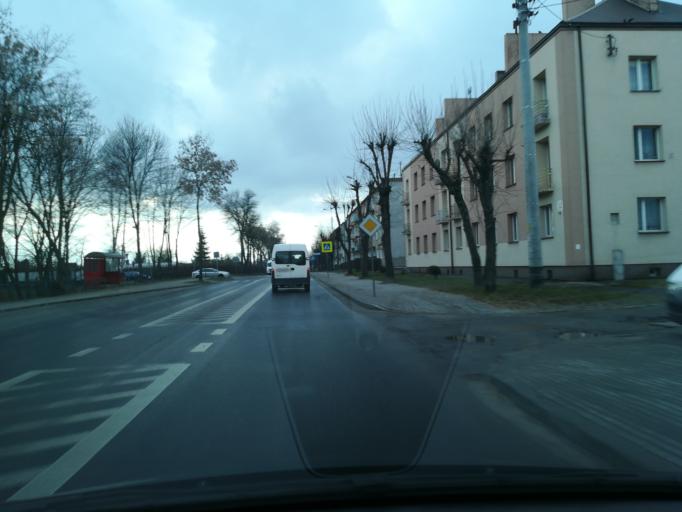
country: PL
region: Lodz Voivodeship
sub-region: Powiat radomszczanski
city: Radomsko
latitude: 51.0712
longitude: 19.4257
